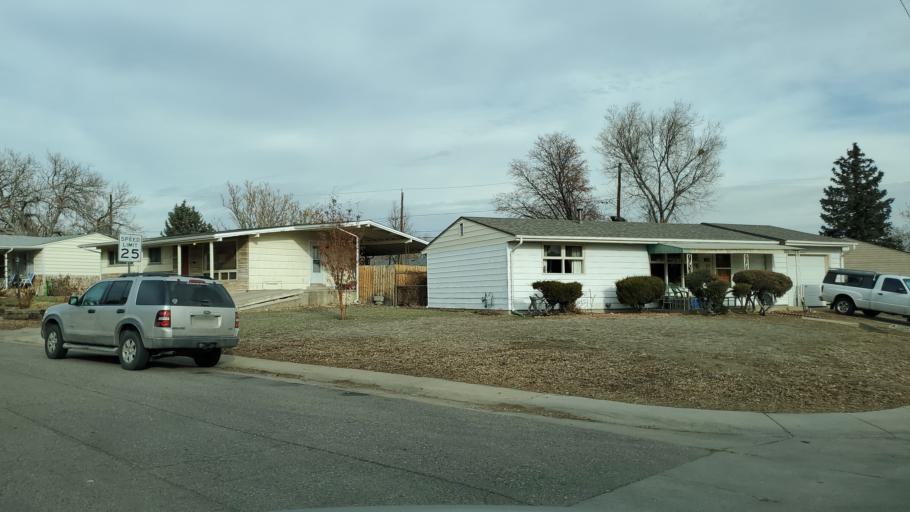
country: US
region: Colorado
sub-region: Adams County
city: Westminster
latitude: 39.8289
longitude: -105.0220
